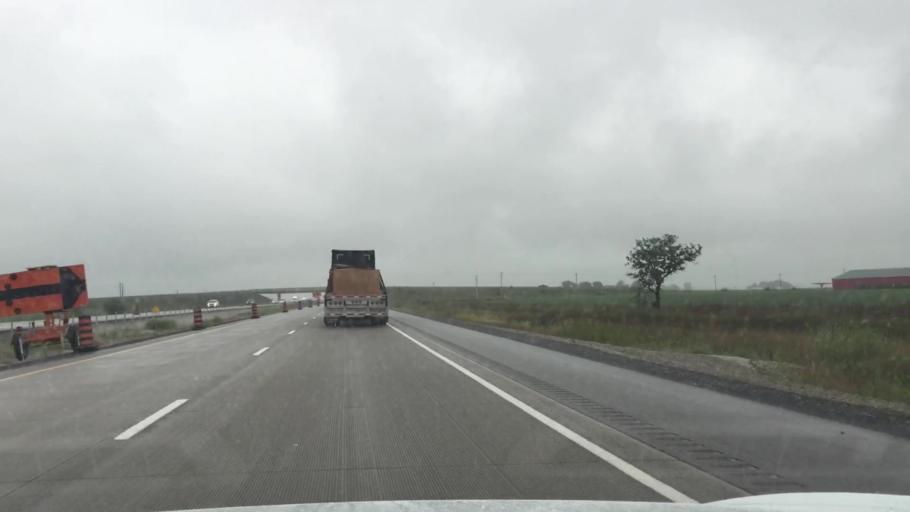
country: CA
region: Ontario
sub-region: Lambton County
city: Walpole Island
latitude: 42.3066
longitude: -82.3177
